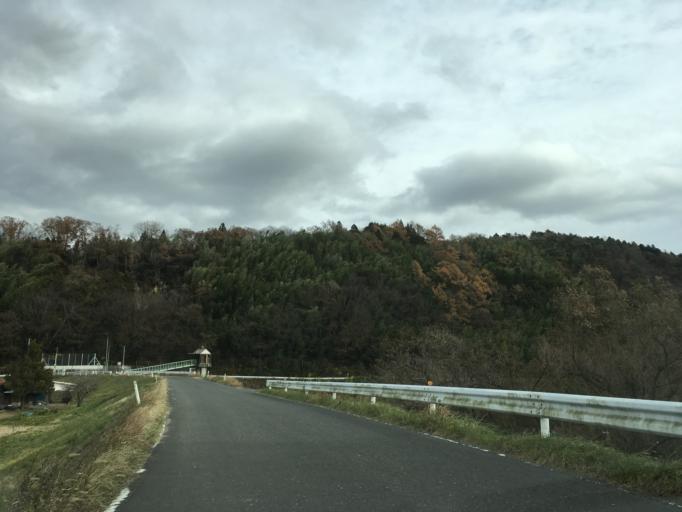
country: JP
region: Iwate
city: Ichinoseki
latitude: 38.7546
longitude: 141.2818
